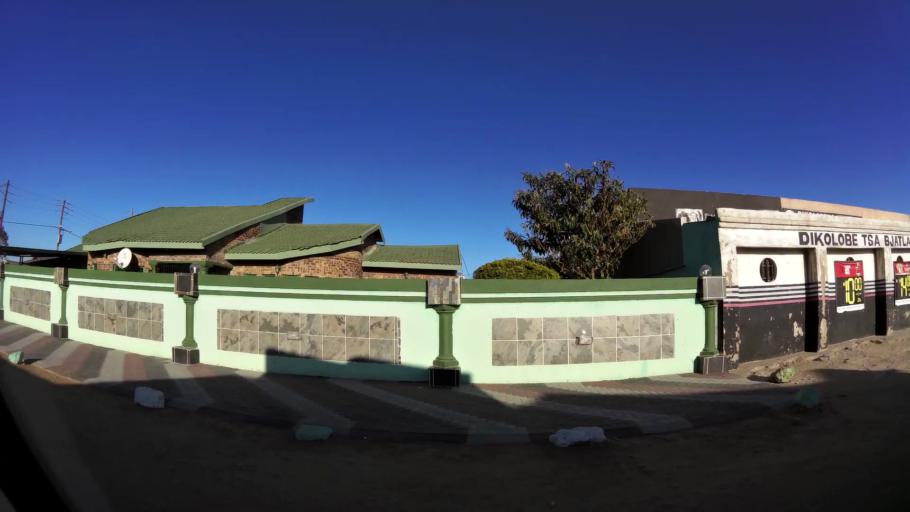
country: ZA
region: Limpopo
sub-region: Capricorn District Municipality
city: Polokwane
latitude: -23.8450
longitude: 29.3569
